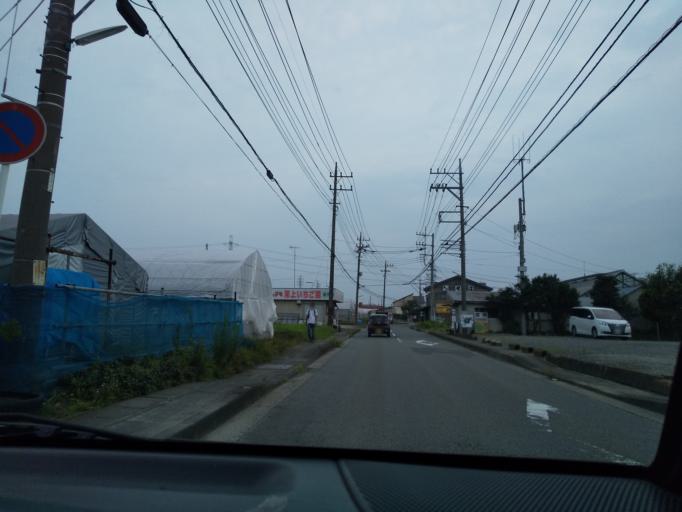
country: JP
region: Kanagawa
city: Atsugi
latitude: 35.4192
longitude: 139.3919
